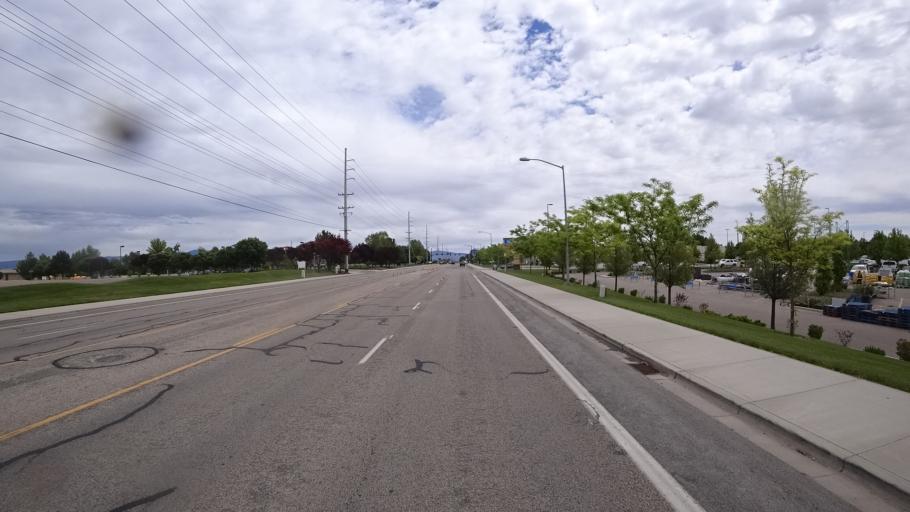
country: US
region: Idaho
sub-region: Ada County
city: Meridian
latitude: 43.5900
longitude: -116.4015
